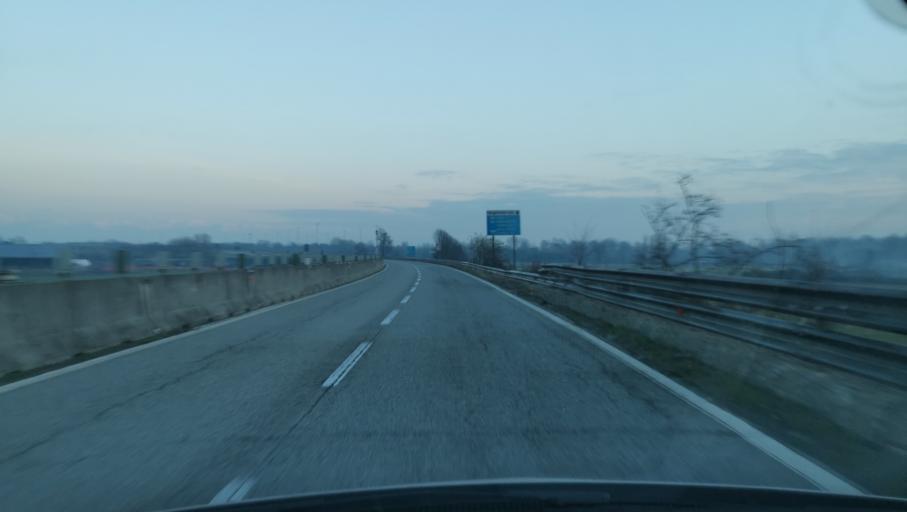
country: IT
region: Piedmont
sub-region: Provincia di Torino
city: Brandizzo
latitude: 45.1816
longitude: 7.8590
